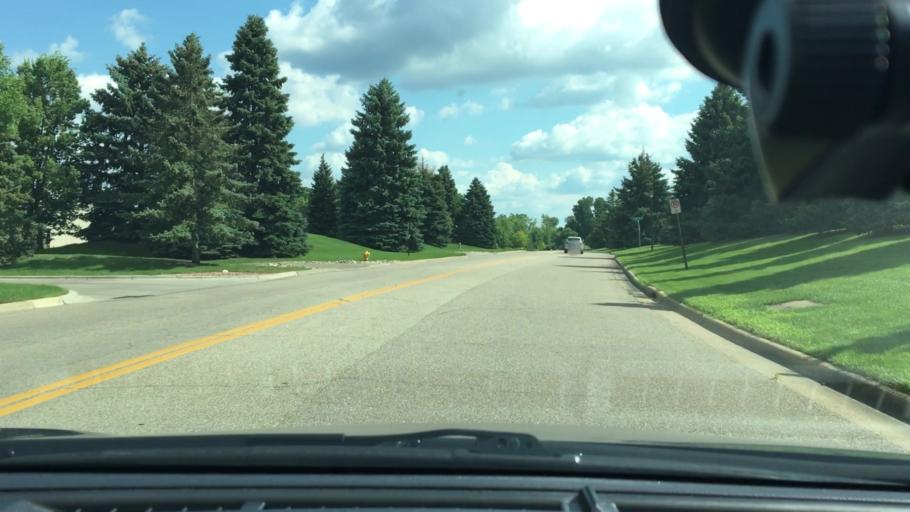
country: US
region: Minnesota
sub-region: Hennepin County
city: New Hope
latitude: 45.0529
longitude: -93.4057
